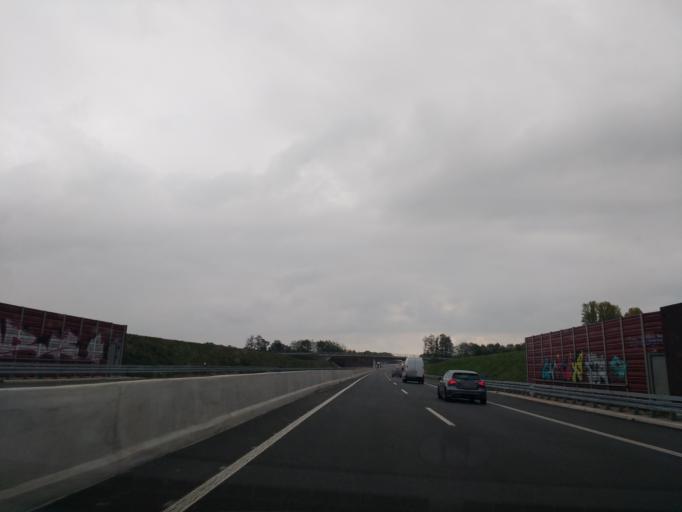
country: DE
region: North Rhine-Westphalia
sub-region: Regierungsbezirk Detmold
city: Steinhagen
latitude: 51.9853
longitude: 8.4552
